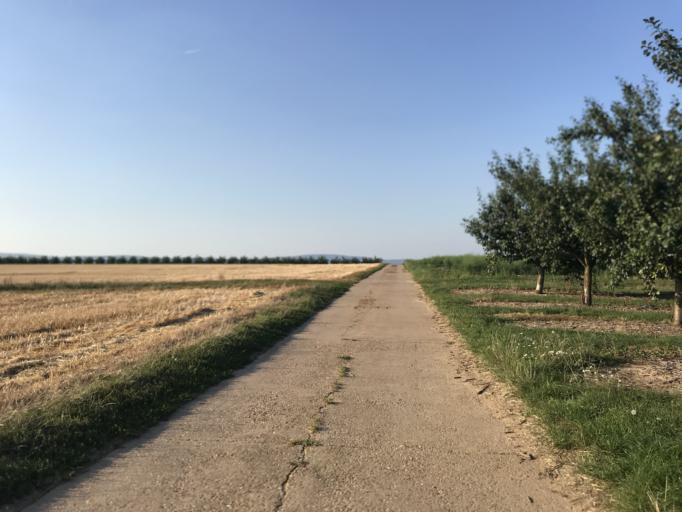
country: DE
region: Rheinland-Pfalz
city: Essenheim
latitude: 49.9517
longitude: 8.1508
